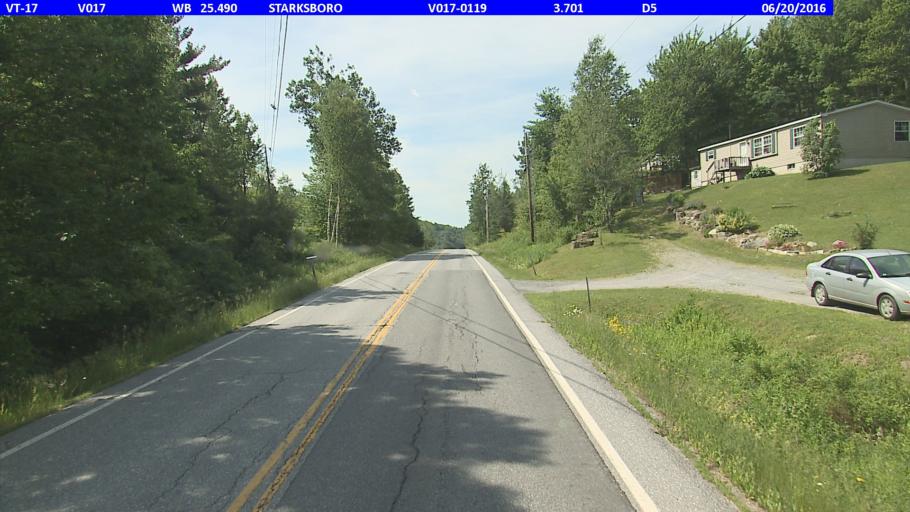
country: US
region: Vermont
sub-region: Addison County
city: Bristol
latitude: 44.1926
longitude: -72.9668
